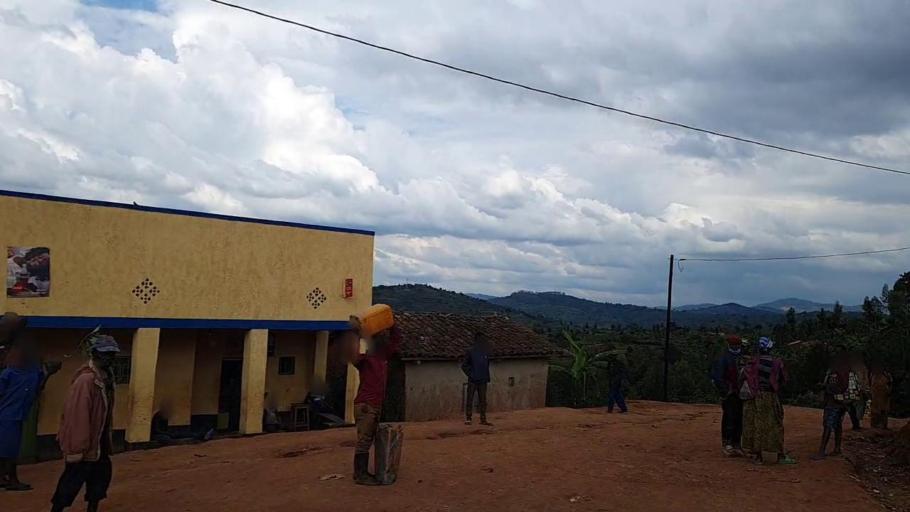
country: RW
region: Southern Province
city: Gikongoro
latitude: -2.4212
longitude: 29.6494
